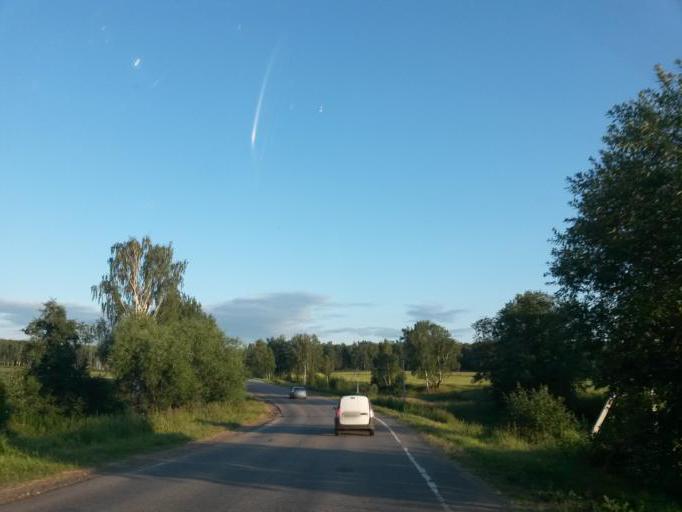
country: RU
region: Moskovskaya
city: Vostryakovo
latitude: 55.3470
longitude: 37.7275
